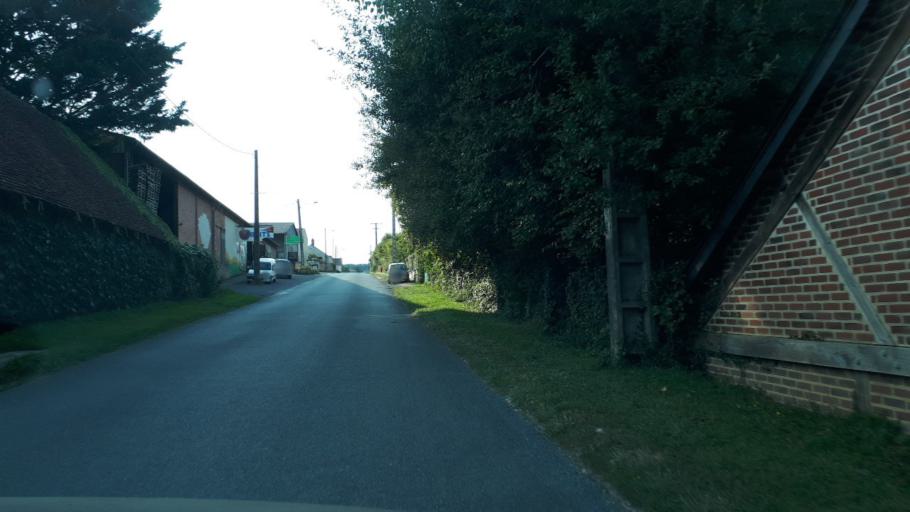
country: FR
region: Centre
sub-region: Departement du Cher
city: Vasselay
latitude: 47.2121
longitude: 2.3904
